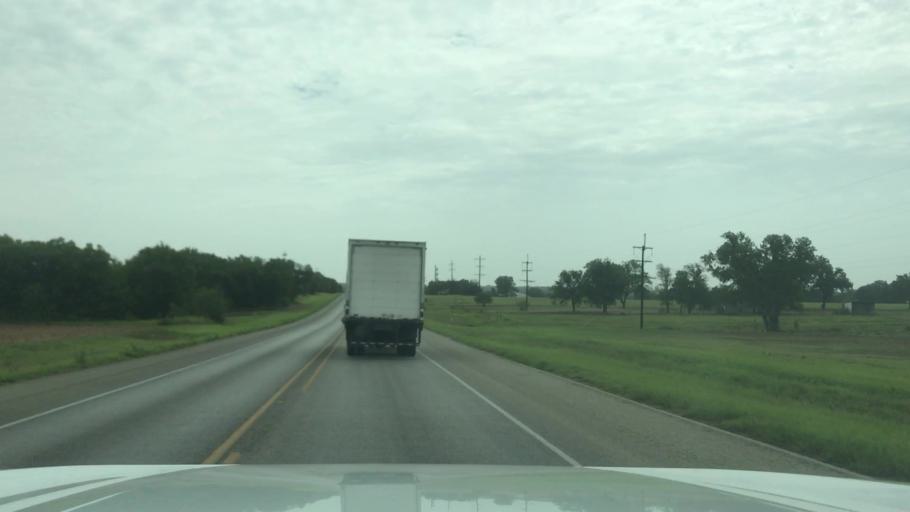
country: US
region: Texas
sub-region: Comanche County
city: De Leon
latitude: 32.0979
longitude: -98.4652
